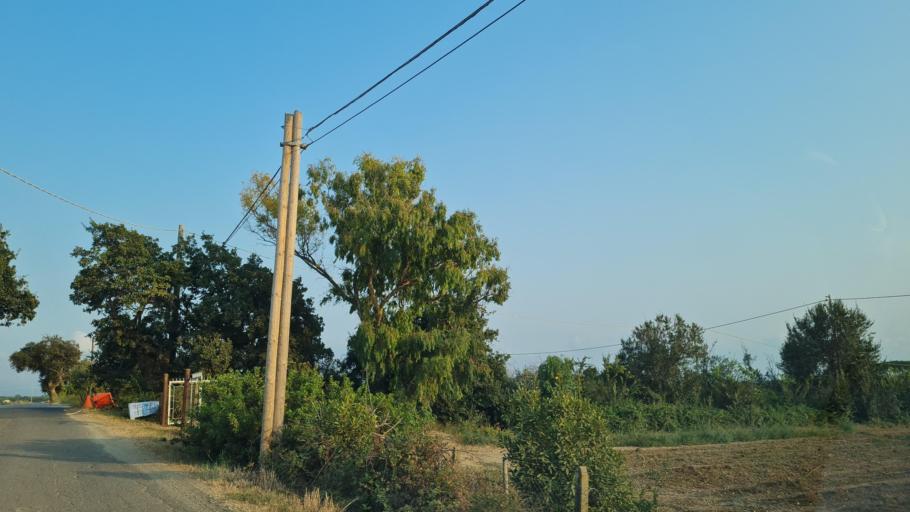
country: IT
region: Latium
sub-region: Provincia di Viterbo
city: Montalto di Castro
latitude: 42.3086
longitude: 11.6215
